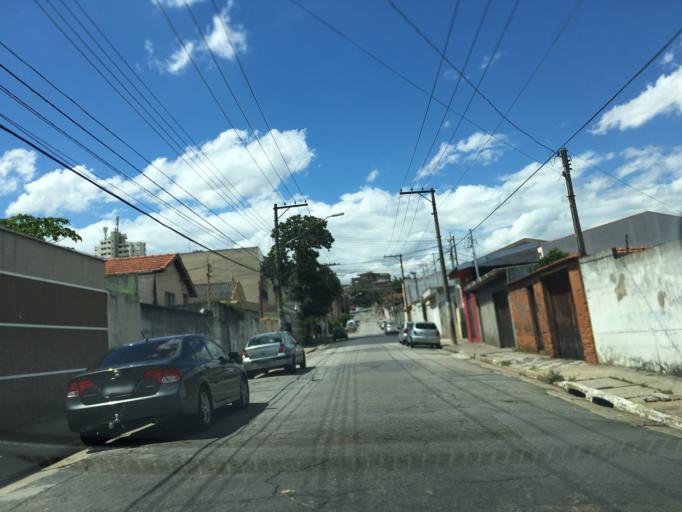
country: BR
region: Sao Paulo
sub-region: Sao Caetano Do Sul
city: Sao Caetano do Sul
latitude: -23.5759
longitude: -46.5624
